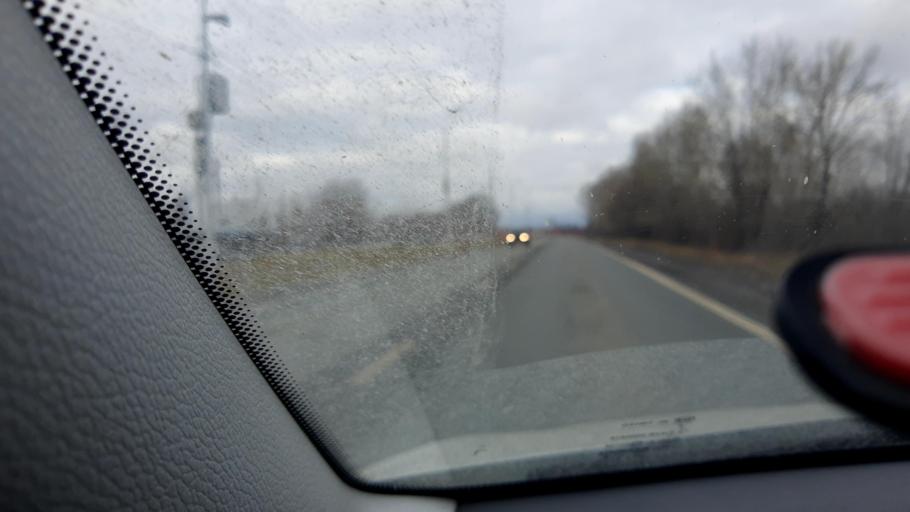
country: RU
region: Bashkortostan
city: Ufa
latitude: 54.8569
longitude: 56.1148
